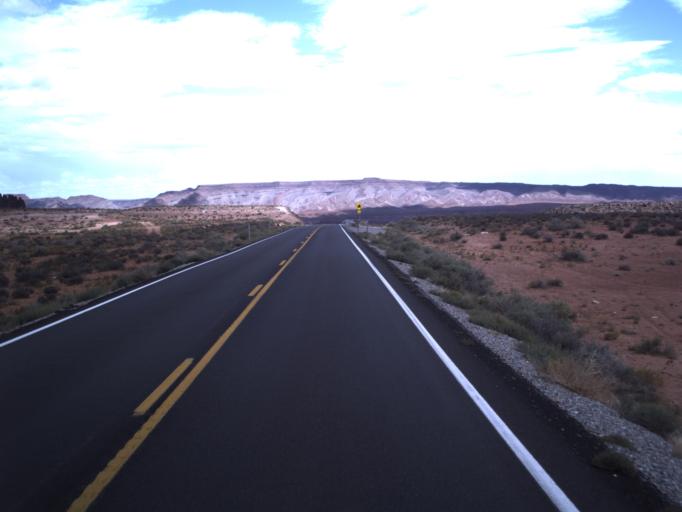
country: US
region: Arizona
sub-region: Navajo County
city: Kayenta
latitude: 37.1258
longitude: -109.9257
